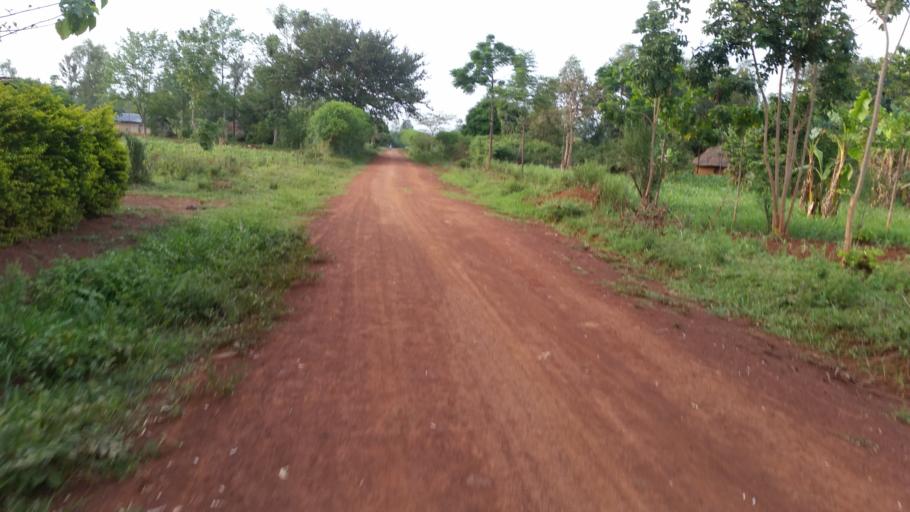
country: UG
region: Eastern Region
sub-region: Busia District
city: Busia
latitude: 0.5311
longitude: 34.0427
